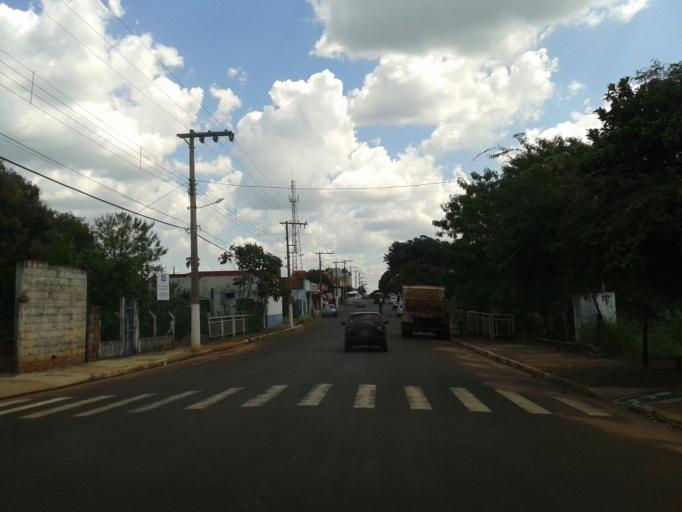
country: BR
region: Minas Gerais
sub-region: Ituiutaba
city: Ituiutaba
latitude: -19.2139
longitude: -49.7844
